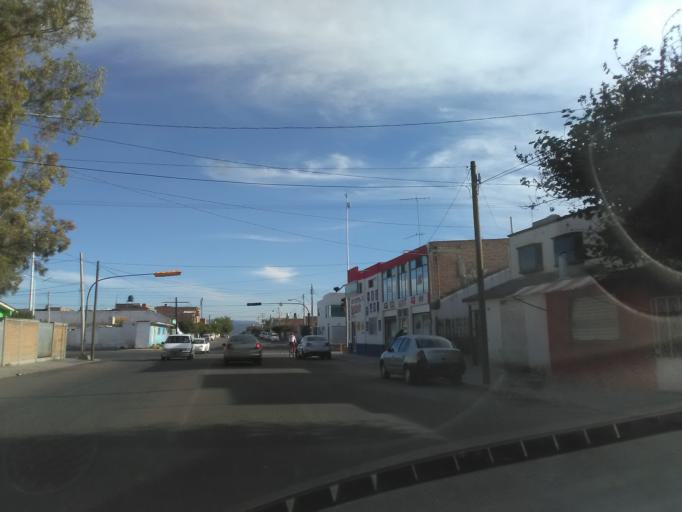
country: MX
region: Durango
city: Victoria de Durango
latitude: 24.0275
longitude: -104.6313
